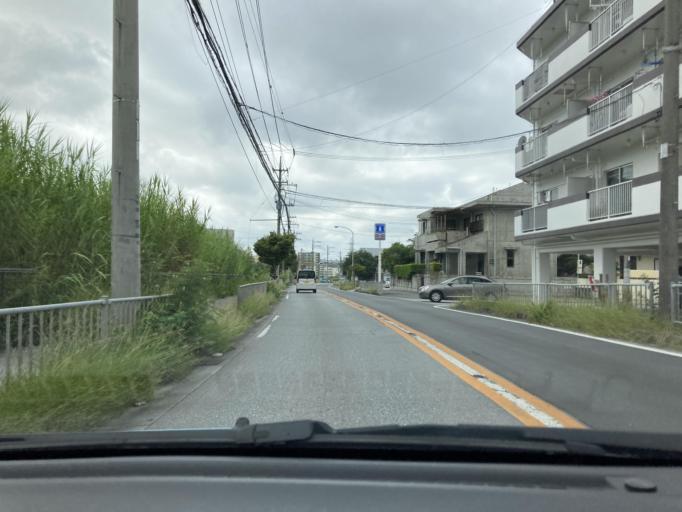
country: JP
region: Okinawa
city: Ginowan
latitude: 26.2417
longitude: 127.7535
